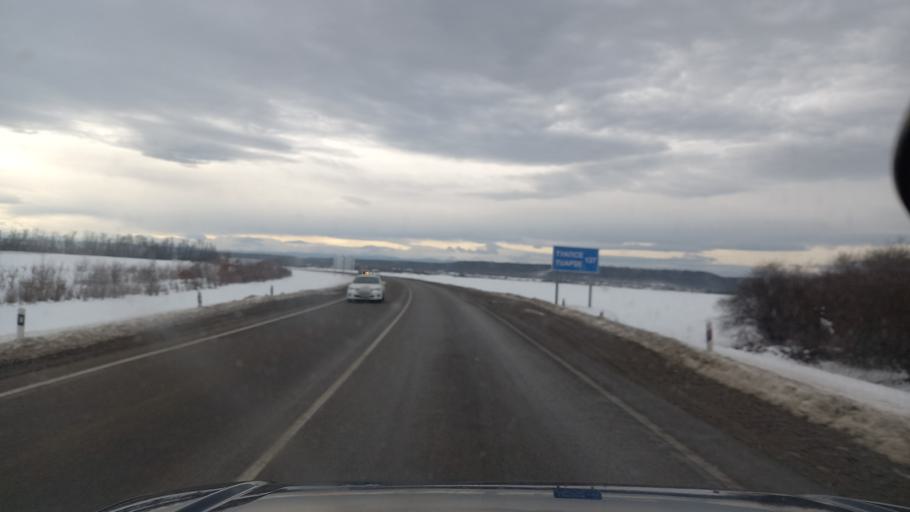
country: RU
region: Adygeya
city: Maykop
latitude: 44.6227
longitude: 40.0391
